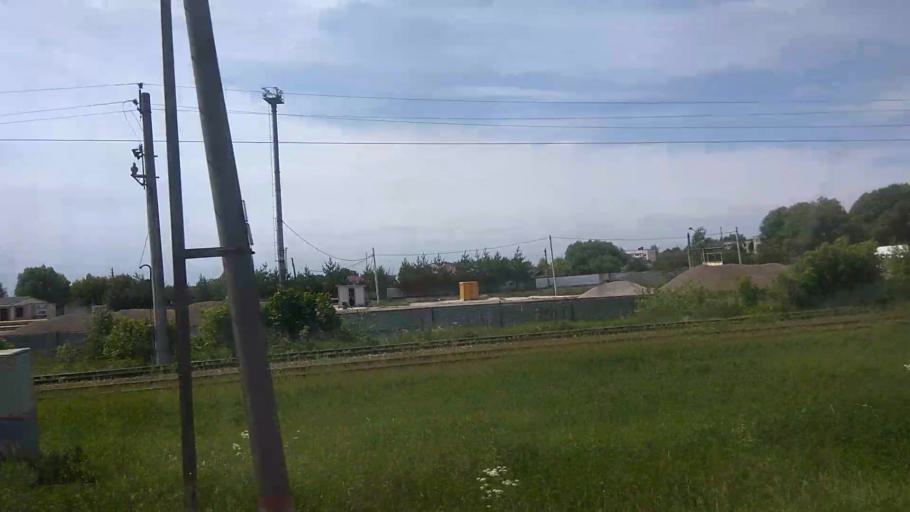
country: RU
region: Moskovskaya
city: Malyshevo
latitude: 55.5078
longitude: 38.3480
